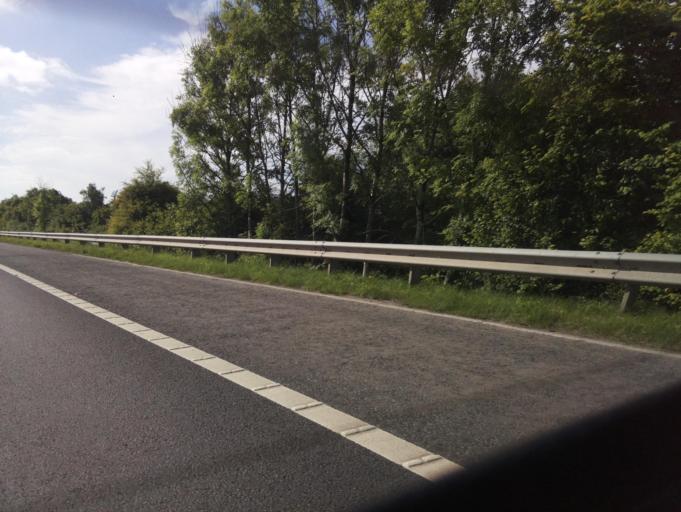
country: GB
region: England
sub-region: Borough of Wigan
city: Tyldesley
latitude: 53.5455
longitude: -2.4517
